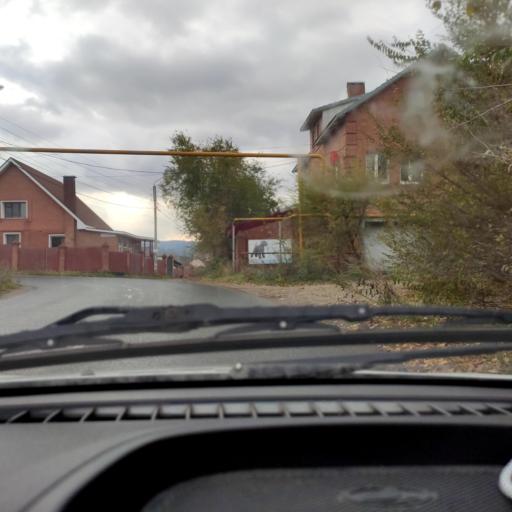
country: RU
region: Samara
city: Zhigulevsk
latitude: 53.4653
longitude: 49.6207
